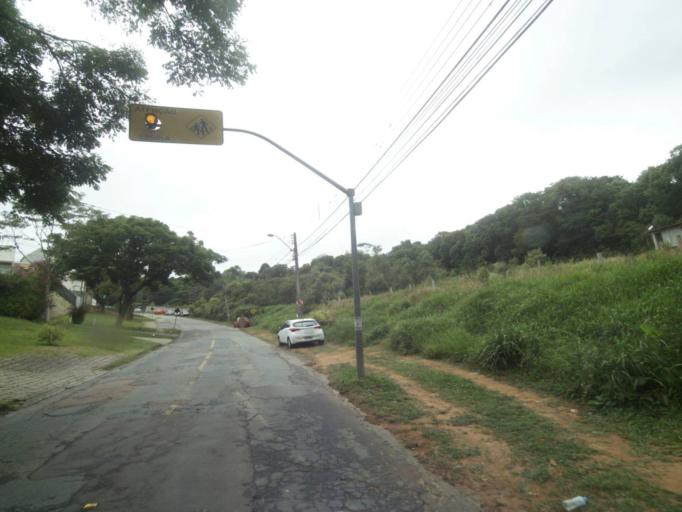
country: BR
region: Parana
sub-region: Curitiba
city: Curitiba
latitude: -25.4232
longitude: -49.3388
